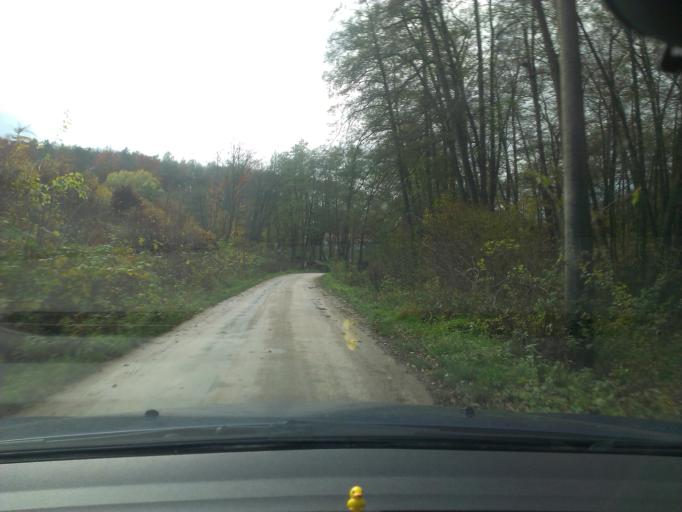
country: SK
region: Trnavsky
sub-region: Okres Trnava
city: Piestany
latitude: 48.6073
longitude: 17.8974
